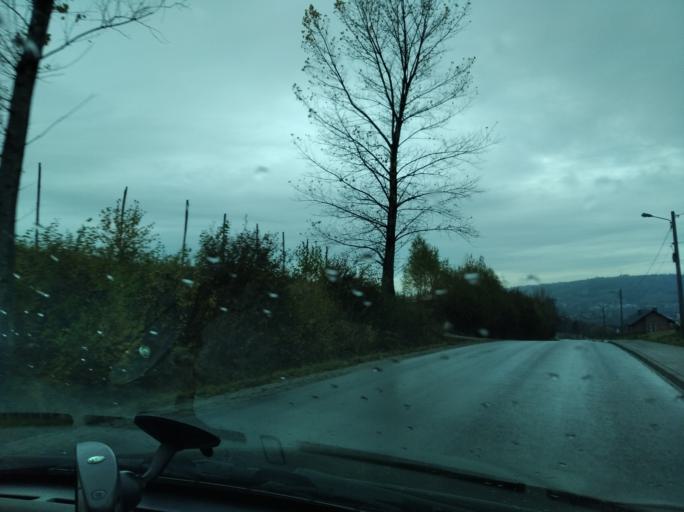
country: PL
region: Subcarpathian Voivodeship
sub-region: Powiat rzeszowski
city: Tyczyn
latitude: 49.9521
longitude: 22.0374
